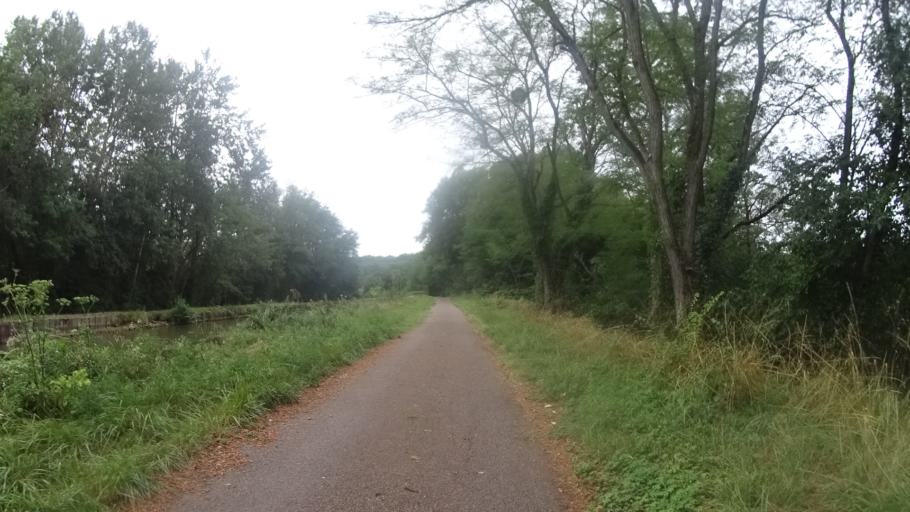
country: FR
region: Bourgogne
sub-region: Departement de la Nievre
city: Saint-Leger-des-Vignes
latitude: 46.8121
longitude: 3.3785
